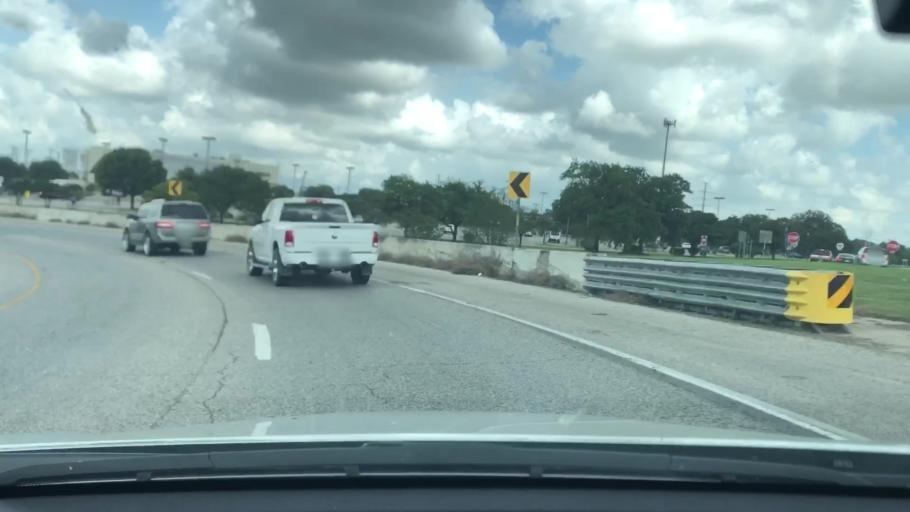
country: US
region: Texas
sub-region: Bexar County
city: Windcrest
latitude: 29.5226
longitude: -98.3923
